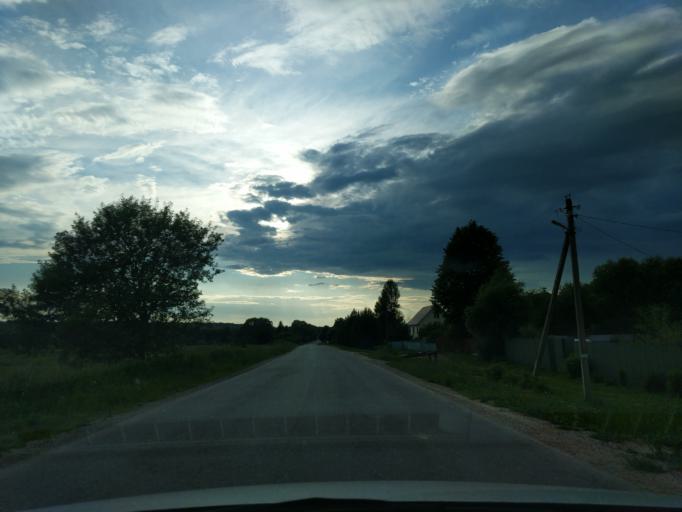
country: RU
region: Kaluga
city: Myatlevo
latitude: 54.8299
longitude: 35.6510
